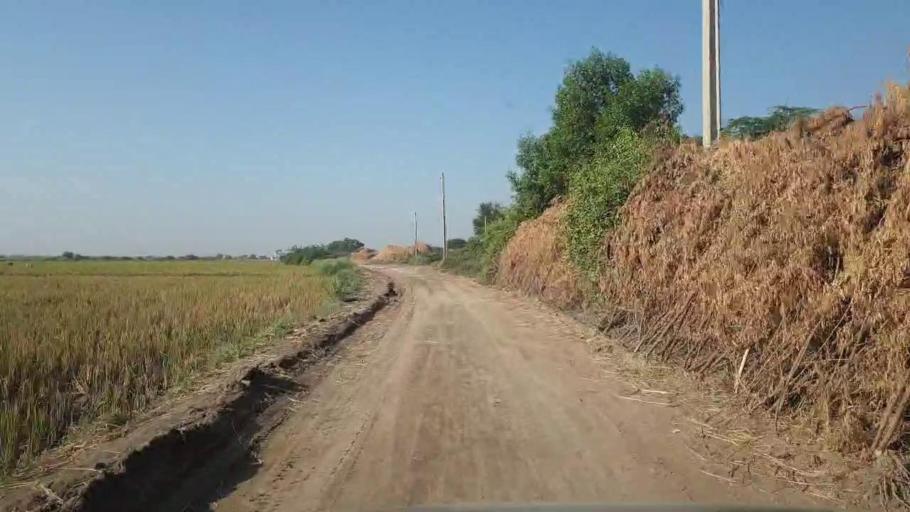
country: PK
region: Sindh
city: Badin
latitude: 24.7127
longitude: 68.7866
